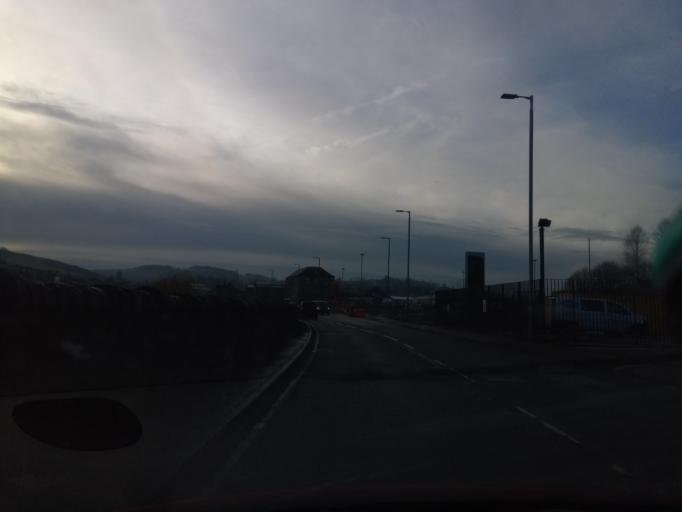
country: GB
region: Scotland
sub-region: The Scottish Borders
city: Hawick
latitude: 55.4267
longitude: -2.7870
